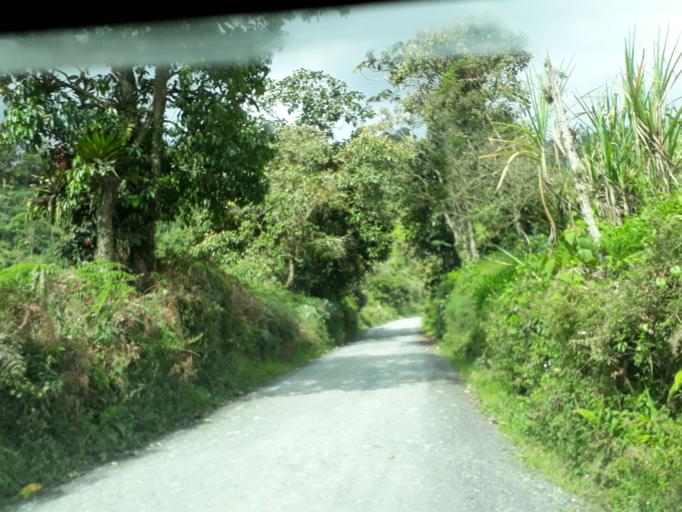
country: CO
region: Cundinamarca
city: Pacho
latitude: 5.2604
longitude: -74.1866
